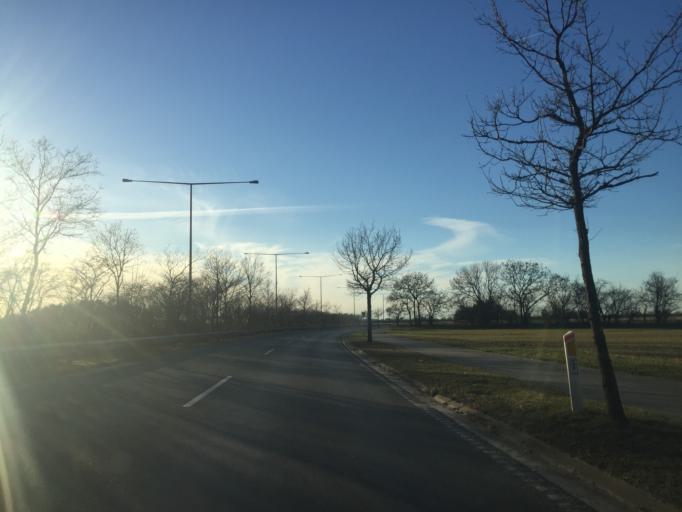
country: DK
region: Capital Region
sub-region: Dragor Kommune
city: Dragor
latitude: 55.5968
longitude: 12.6287
